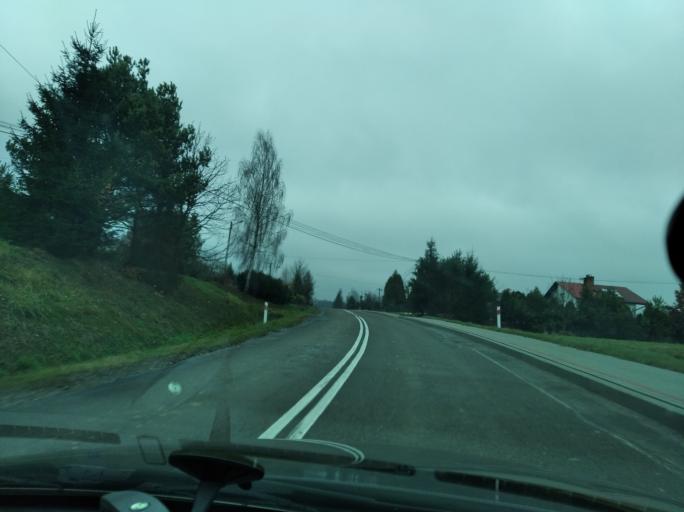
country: PL
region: Subcarpathian Voivodeship
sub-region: Powiat przeworski
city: Jawornik Polski
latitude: 49.8713
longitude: 22.2461
